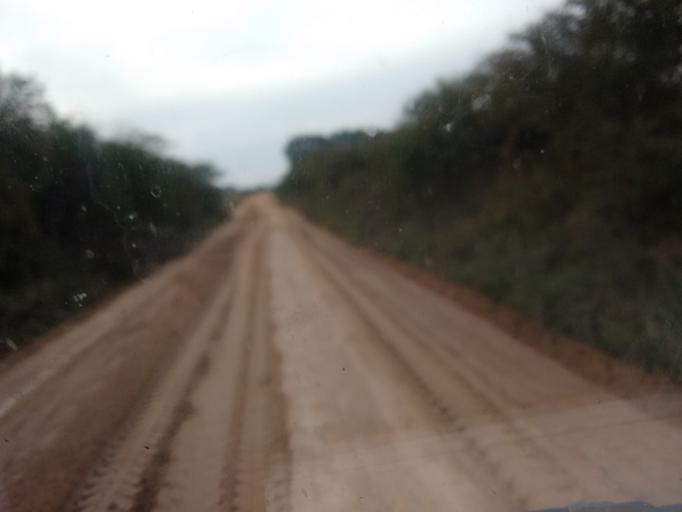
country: BR
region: Rio Grande do Sul
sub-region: Camaqua
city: Camaqua
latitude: -31.1495
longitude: -51.7594
